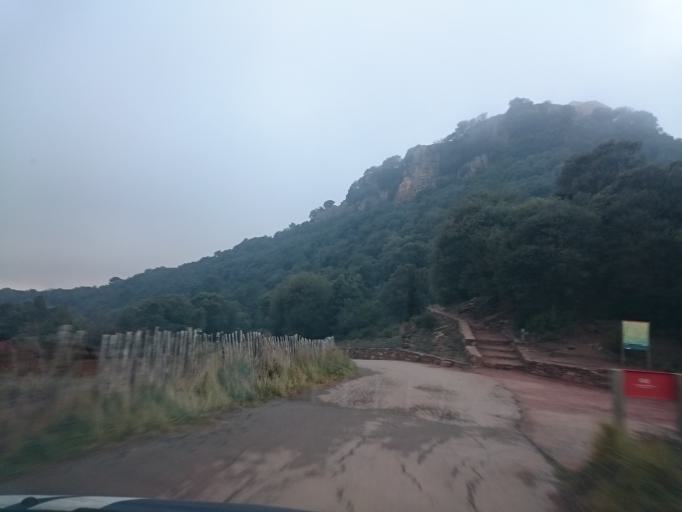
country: ES
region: Catalonia
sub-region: Provincia de Barcelona
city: Tagamanent
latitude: 41.7479
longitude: 2.2988
